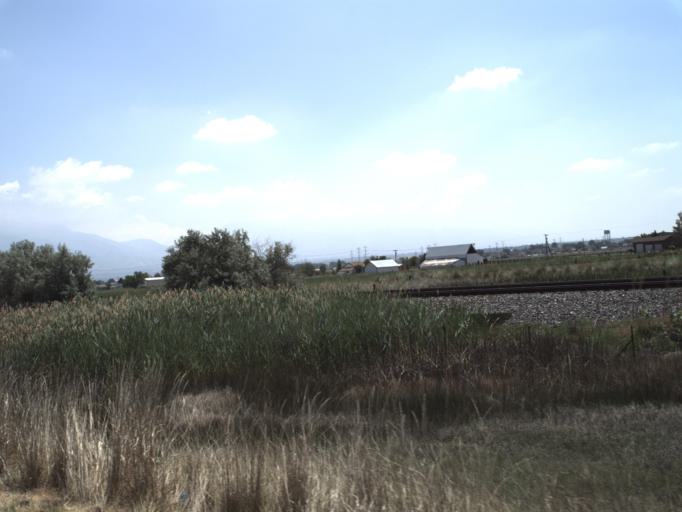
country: US
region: Utah
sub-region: Weber County
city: West Haven
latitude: 41.2444
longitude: -112.0775
